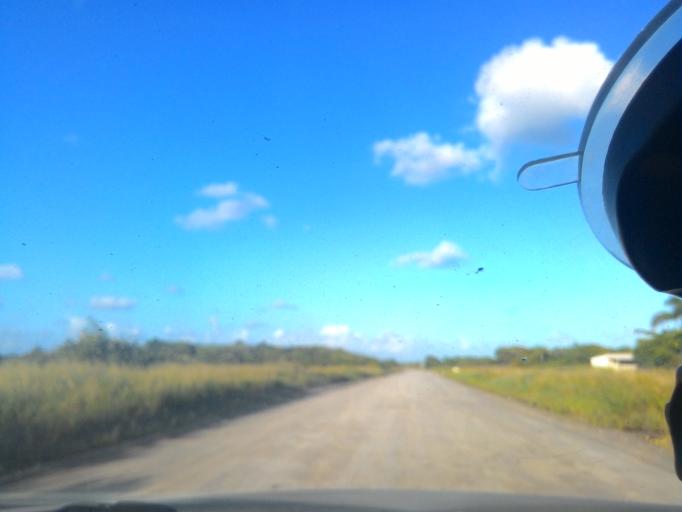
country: BR
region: Sao Paulo
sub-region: Pariquera-Acu
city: Pariquera Acu
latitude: -24.8809
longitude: -47.7373
